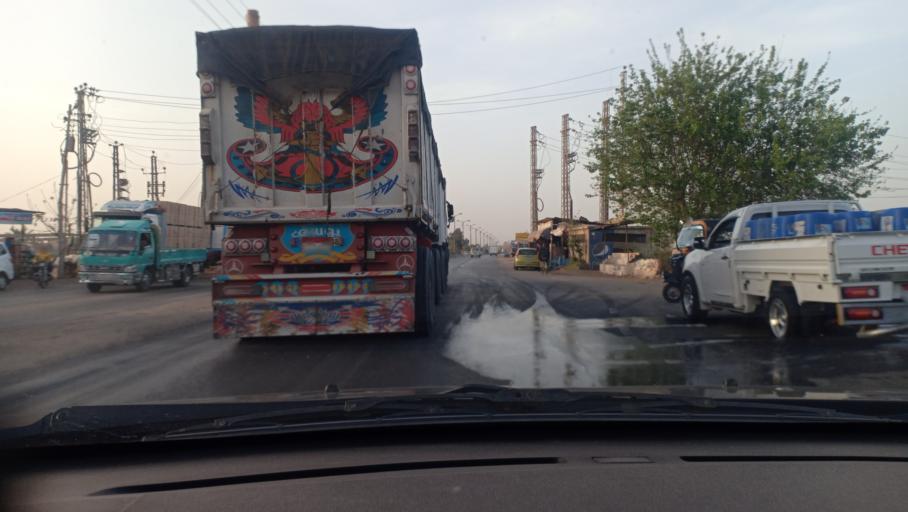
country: EG
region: Muhafazat al Gharbiyah
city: Zifta
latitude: 30.6088
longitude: 31.2754
